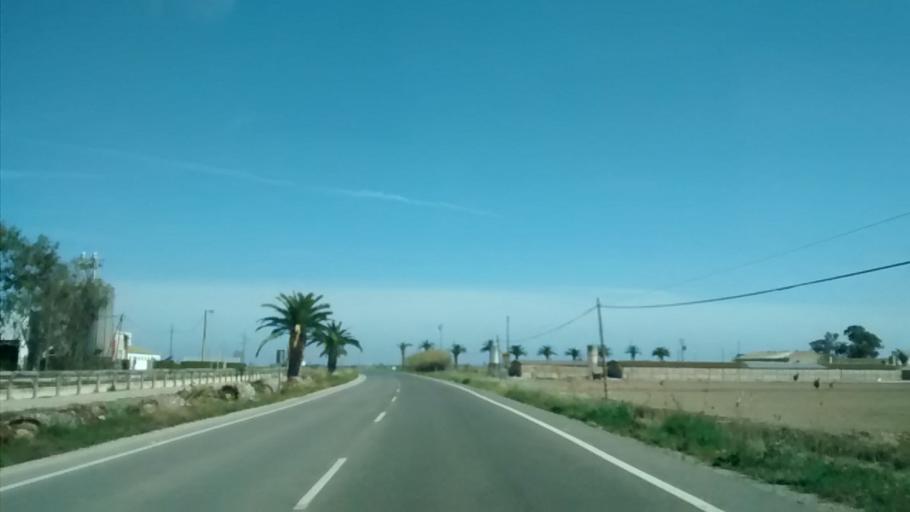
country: ES
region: Catalonia
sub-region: Provincia de Tarragona
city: Deltebre
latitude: 40.7077
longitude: 0.7627
